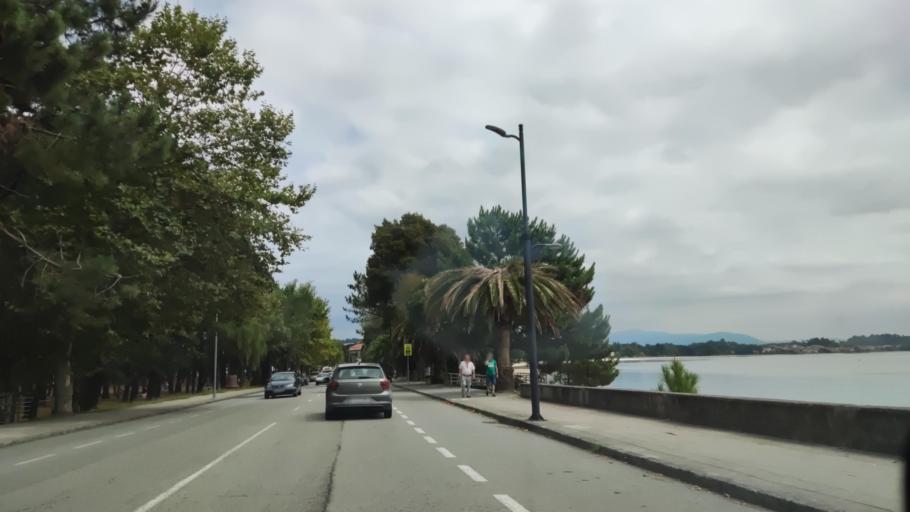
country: ES
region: Galicia
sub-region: Provincia da Coruna
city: Boiro
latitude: 42.6405
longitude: -8.9003
